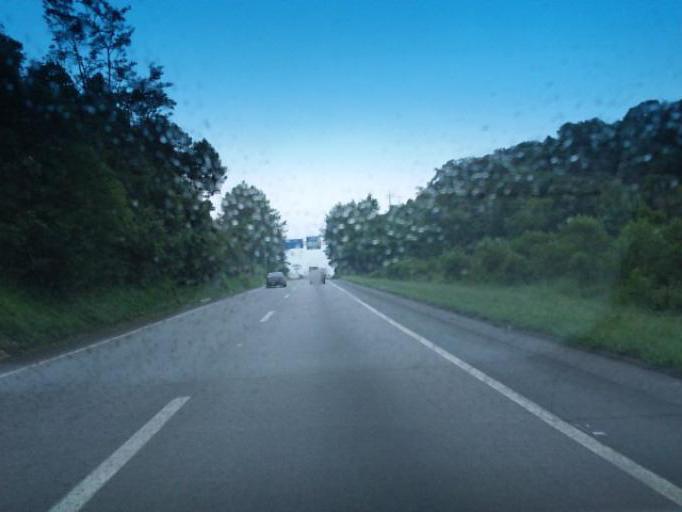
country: BR
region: Parana
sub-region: Campina Grande Do Sul
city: Campina Grande do Sul
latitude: -25.3008
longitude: -48.9406
